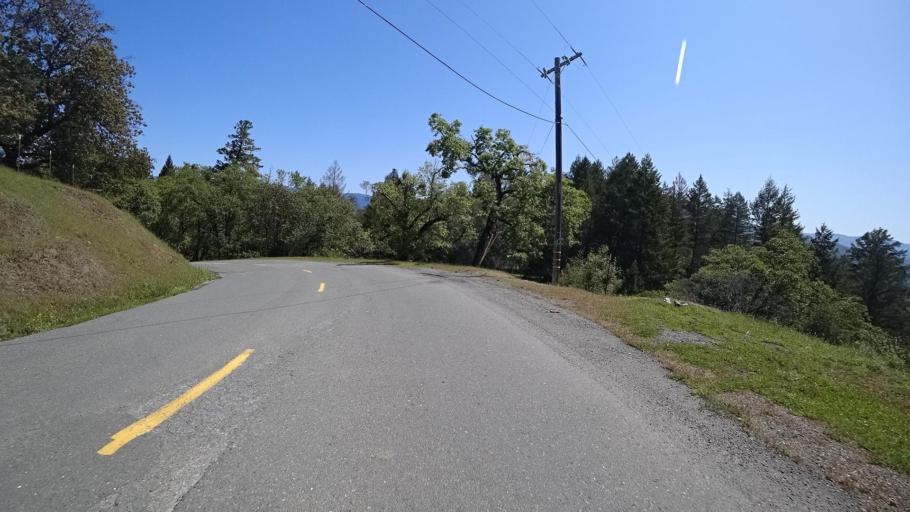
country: US
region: California
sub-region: Humboldt County
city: Redway
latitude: 40.1586
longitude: -123.6170
